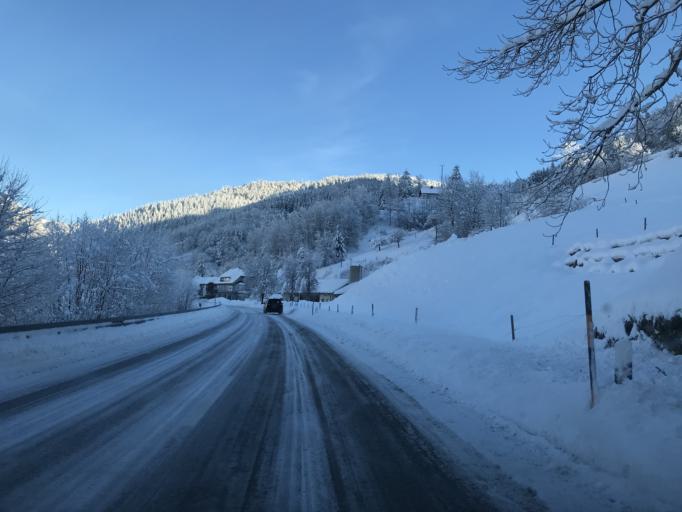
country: DE
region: Baden-Wuerttemberg
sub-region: Freiburg Region
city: Bollen
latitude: 47.7716
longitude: 7.8269
